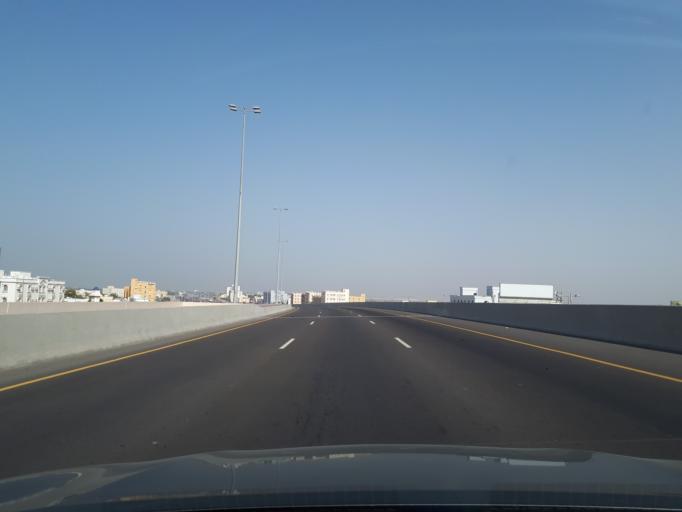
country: OM
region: Al Batinah
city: Al Liwa'
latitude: 24.4239
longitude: 56.6113
